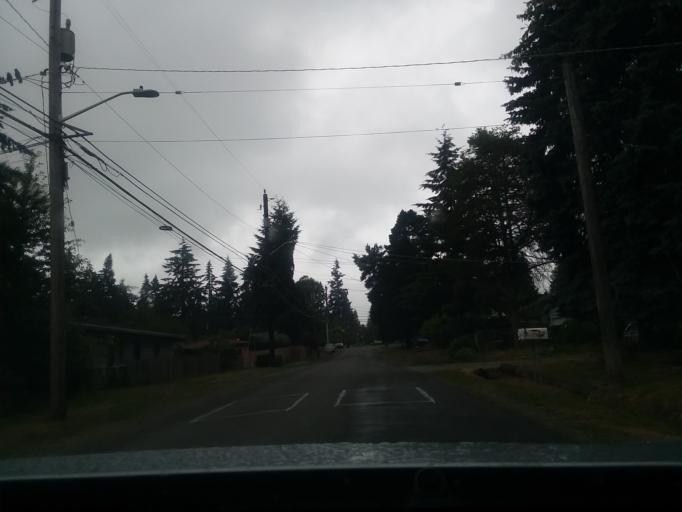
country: US
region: Washington
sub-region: King County
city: Shoreline
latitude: 47.7276
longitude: -122.3396
